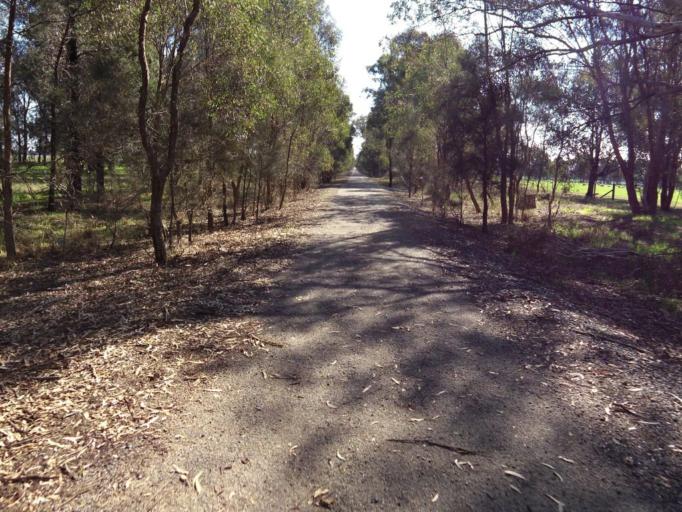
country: AU
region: New South Wales
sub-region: Corowa Shire
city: Corowa
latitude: -36.0315
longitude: 146.4425
